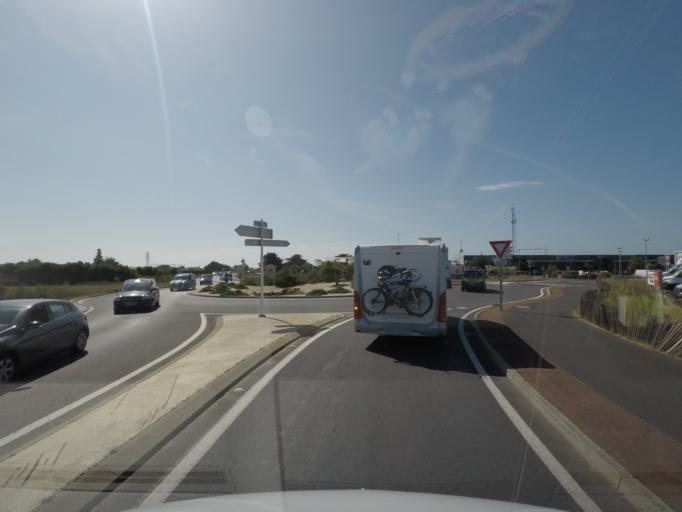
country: FR
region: Pays de la Loire
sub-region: Departement de la Vendee
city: La Gueriniere
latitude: 46.9756
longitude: -2.2410
